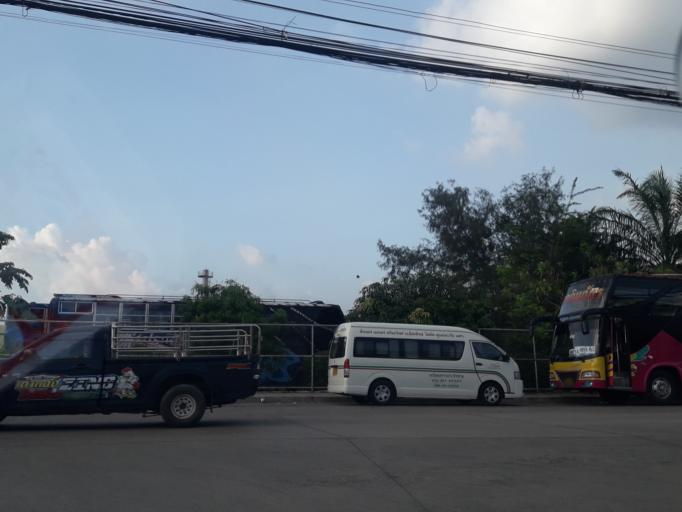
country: TH
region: Phra Nakhon Si Ayutthaya
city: Ban Bang Kadi Pathum Thani
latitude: 13.9982
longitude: 100.6180
